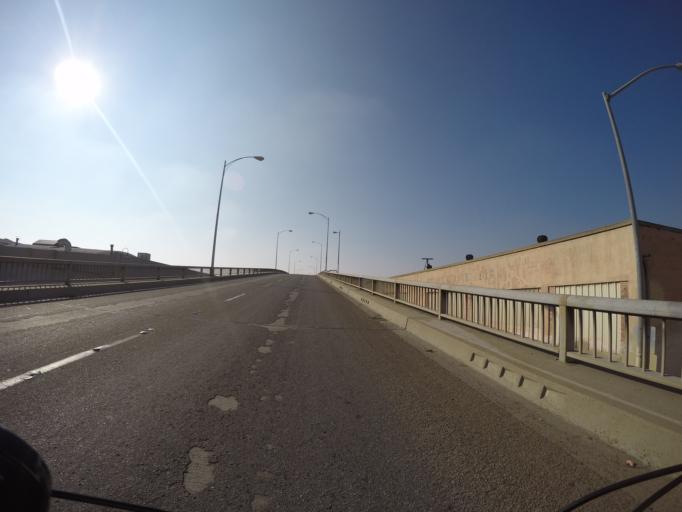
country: US
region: California
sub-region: Fresno County
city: Fresno
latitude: 36.7379
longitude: -119.7970
